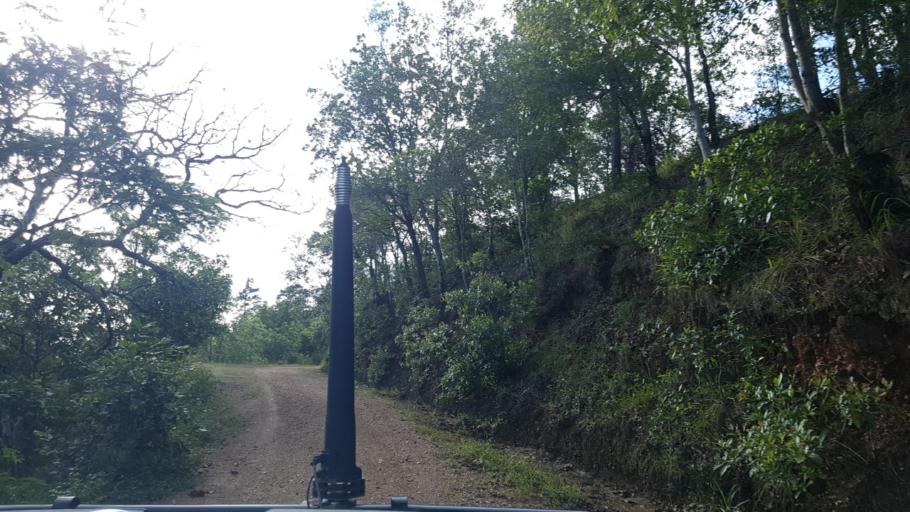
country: NI
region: Nueva Segovia
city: Ciudad Antigua
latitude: 13.6365
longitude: -86.2881
